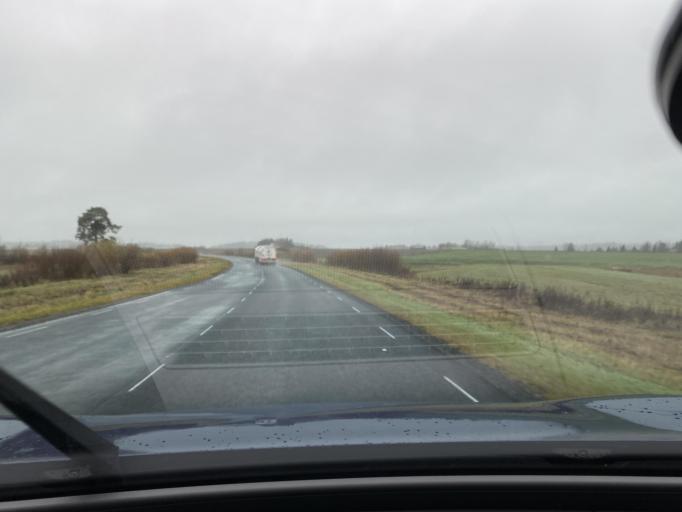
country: FI
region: Haeme
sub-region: Forssa
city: Ypaejae
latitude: 60.7836
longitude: 23.3053
